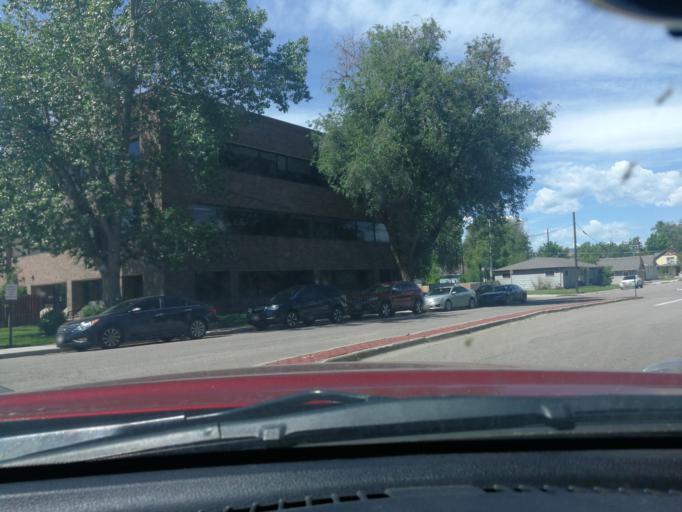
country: US
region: Colorado
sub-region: Arapahoe County
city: Littleton
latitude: 39.6169
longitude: -105.0144
